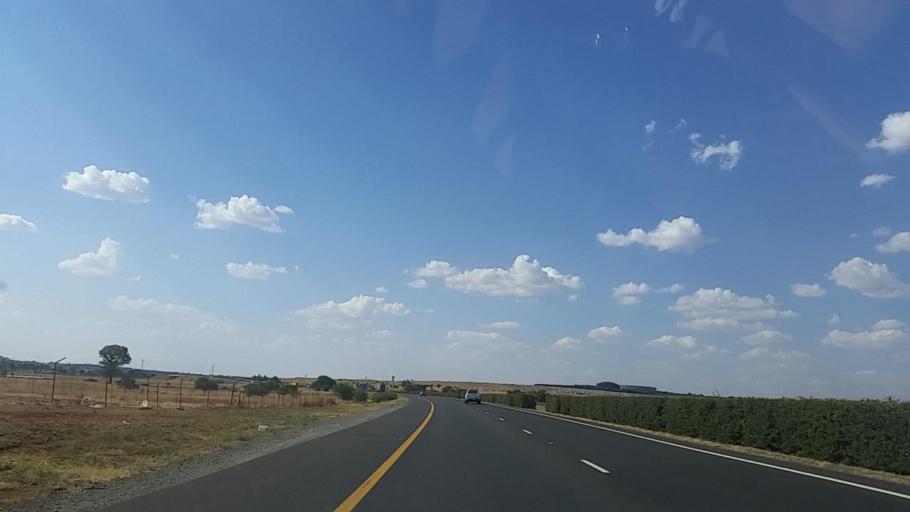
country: ZA
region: Orange Free State
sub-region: Mangaung Metropolitan Municipality
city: Bloemfontein
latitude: -29.1926
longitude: 26.1931
